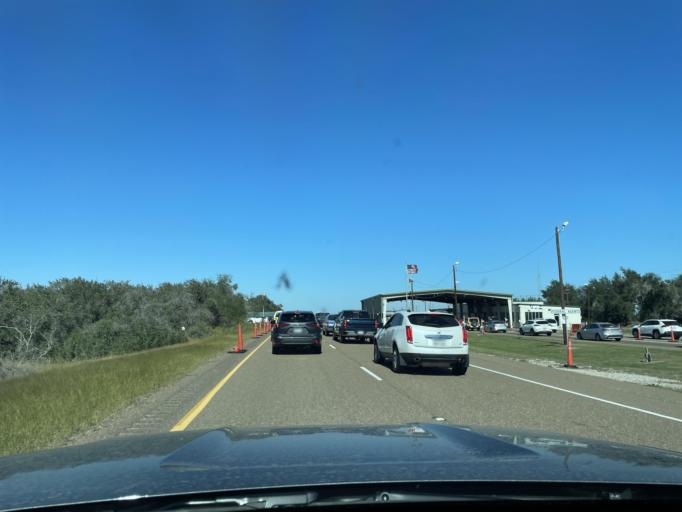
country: US
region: Texas
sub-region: Kenedy County
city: Sarita
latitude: 27.0151
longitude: -97.7944
